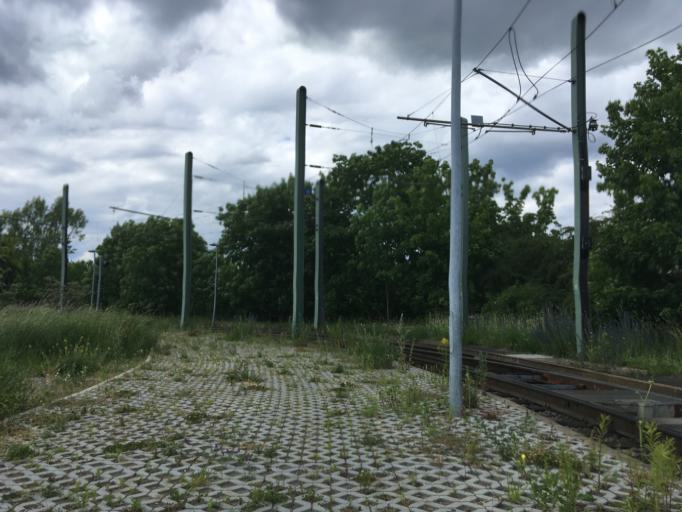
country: DE
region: Berlin
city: Wartenberg
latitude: 52.5703
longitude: 13.5282
